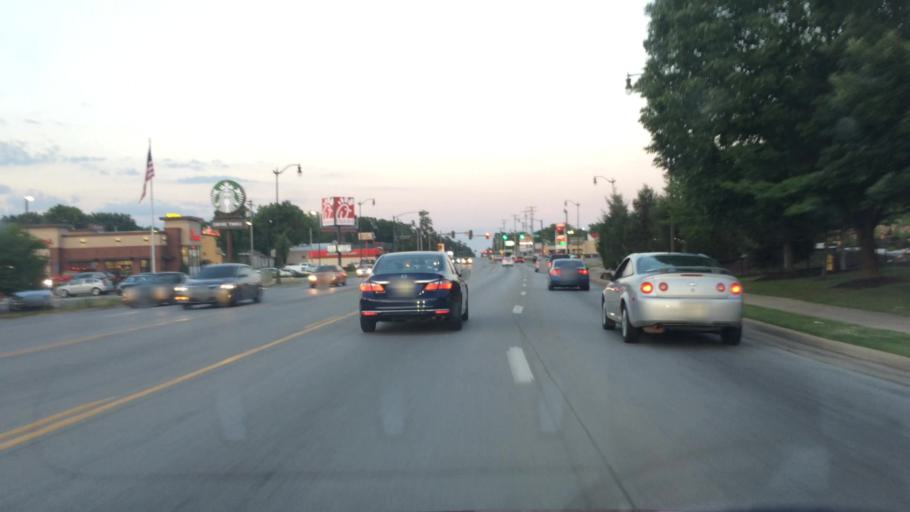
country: US
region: Missouri
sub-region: Greene County
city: Springfield
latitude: 37.1822
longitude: -93.2970
